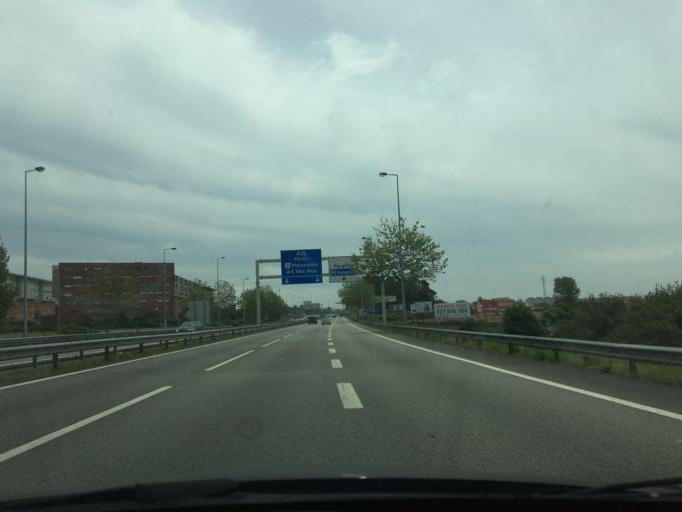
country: PT
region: Porto
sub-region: Matosinhos
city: Santa Cruz do Bispo
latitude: 41.2324
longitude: -8.6955
